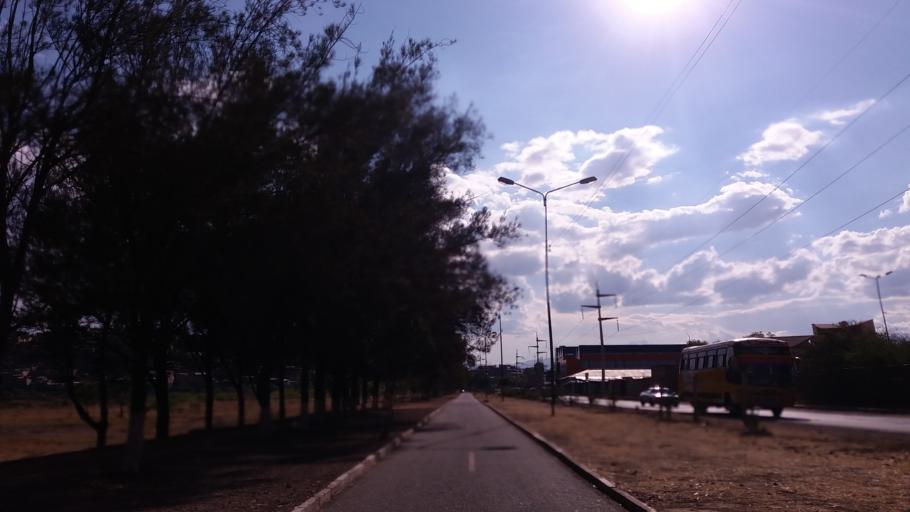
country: BO
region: Cochabamba
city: Cochabamba
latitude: -17.4005
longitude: -66.1411
